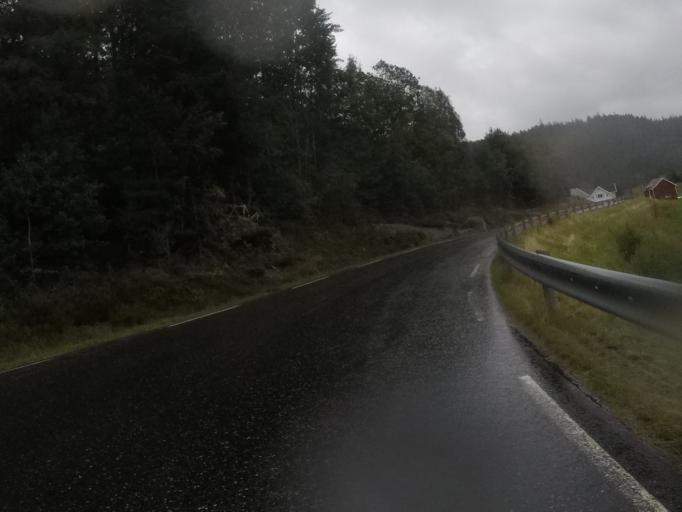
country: NO
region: Vest-Agder
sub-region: Audnedal
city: Konsmo
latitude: 58.2793
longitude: 7.2872
